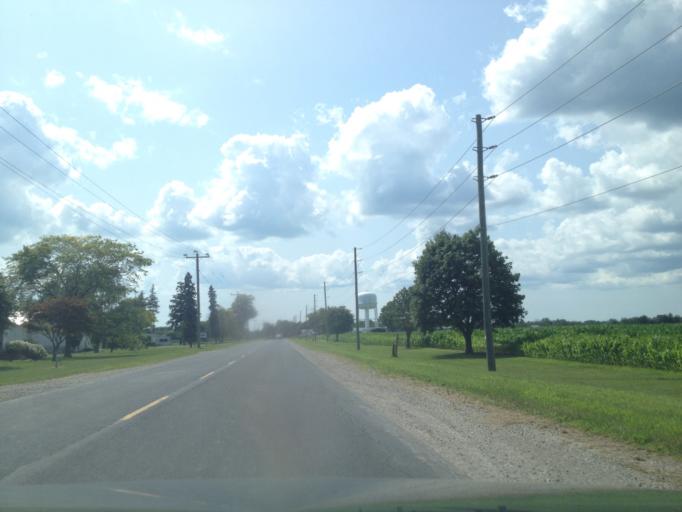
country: CA
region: Ontario
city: Aylmer
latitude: 42.6742
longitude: -80.8898
